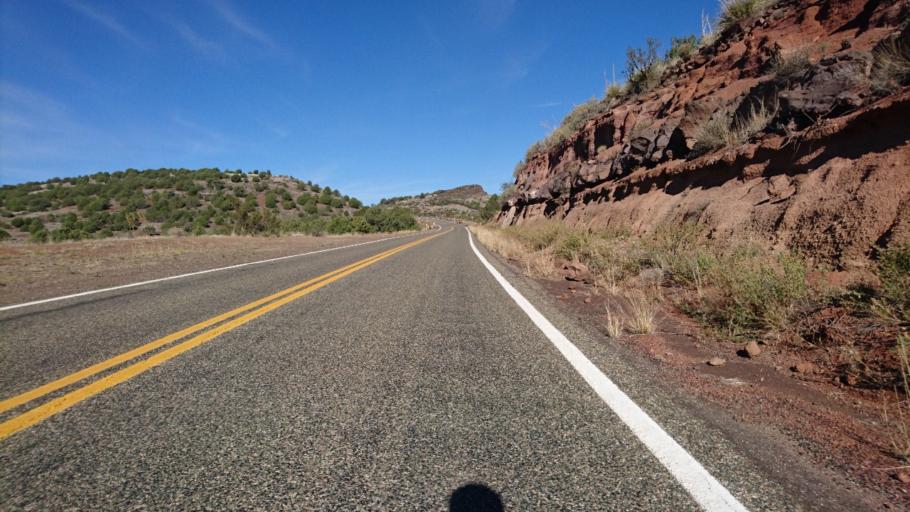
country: US
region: Arizona
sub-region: Yavapai County
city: Paulden
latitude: 35.2747
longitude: -112.6887
